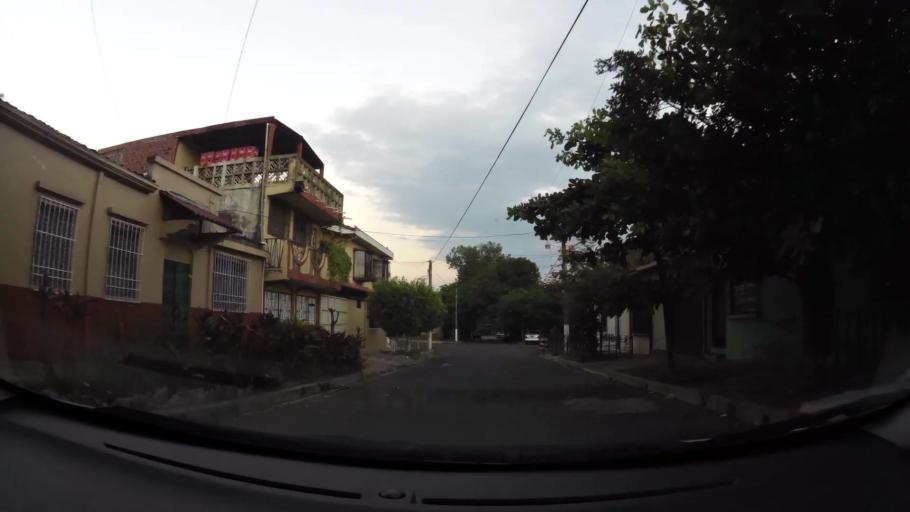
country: SV
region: San Salvador
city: San Salvador
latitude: 13.7060
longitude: -89.1841
